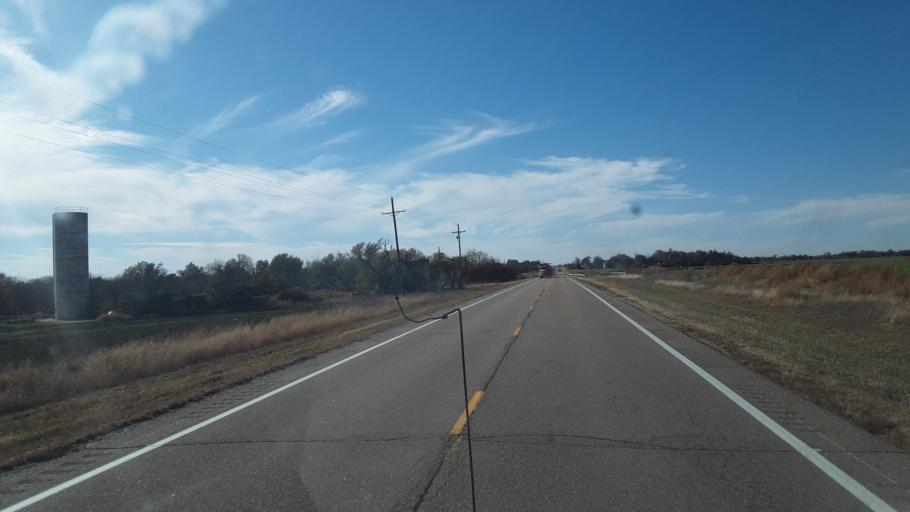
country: US
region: Kansas
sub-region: Pawnee County
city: Larned
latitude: 38.1897
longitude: -99.3195
